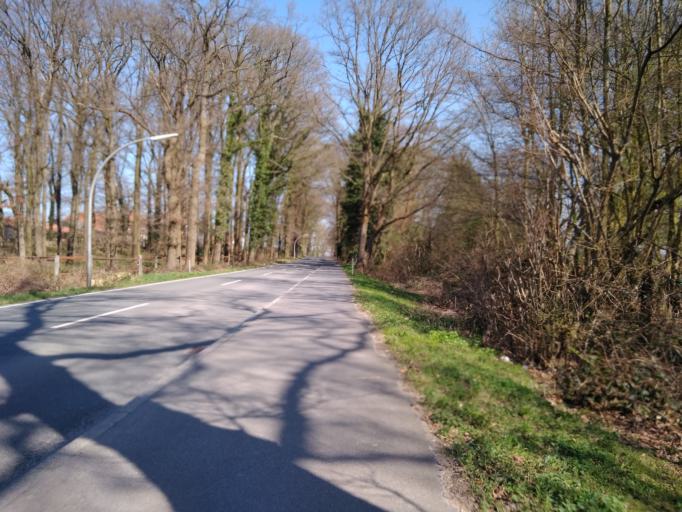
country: DE
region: North Rhine-Westphalia
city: Dorsten
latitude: 51.6531
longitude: 6.9392
